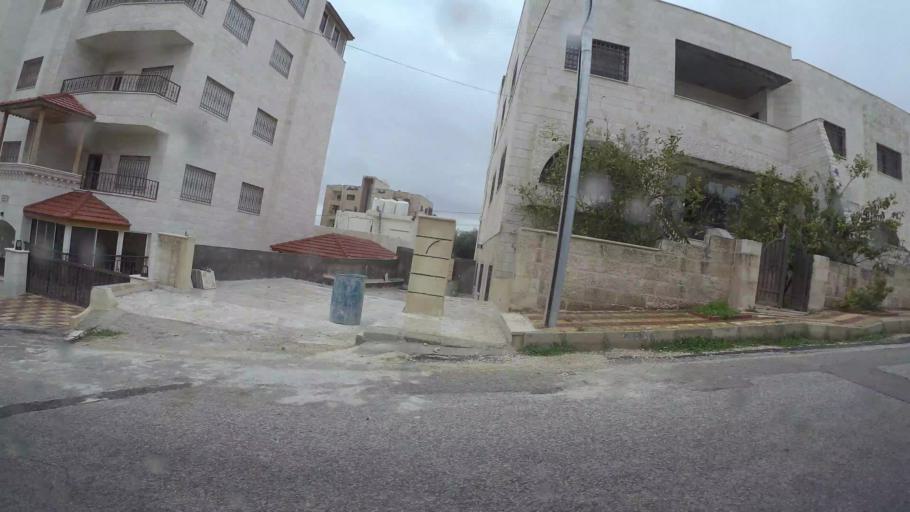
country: JO
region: Amman
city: Al Jubayhah
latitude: 31.9868
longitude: 35.8575
